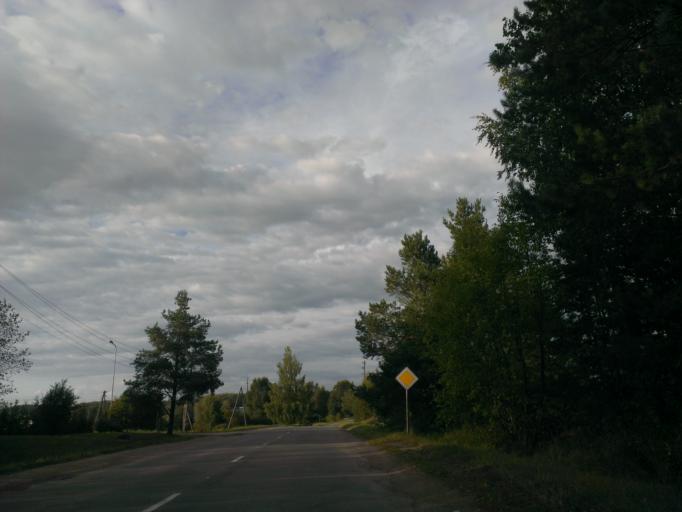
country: LV
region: Ikskile
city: Ikskile
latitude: 56.8431
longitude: 24.5020
